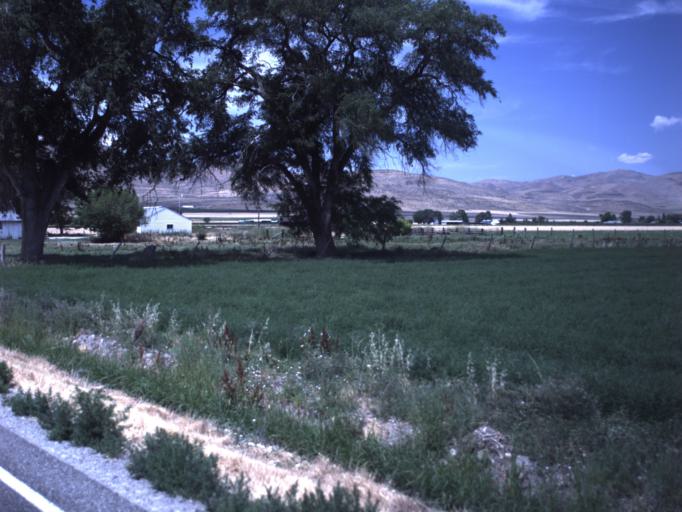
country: US
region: Utah
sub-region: Box Elder County
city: Tremonton
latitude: 41.7095
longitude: -112.2691
